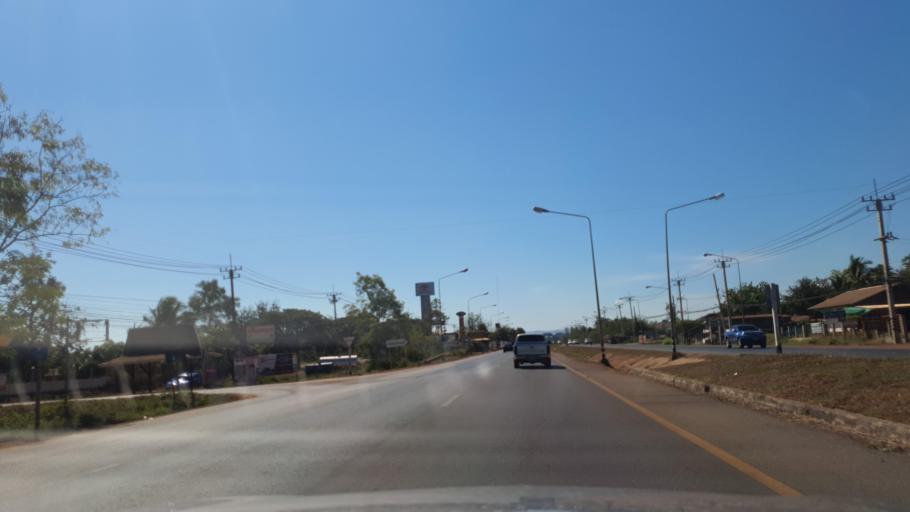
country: TH
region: Sakon Nakhon
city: Sakon Nakhon
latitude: 17.2143
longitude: 104.1031
